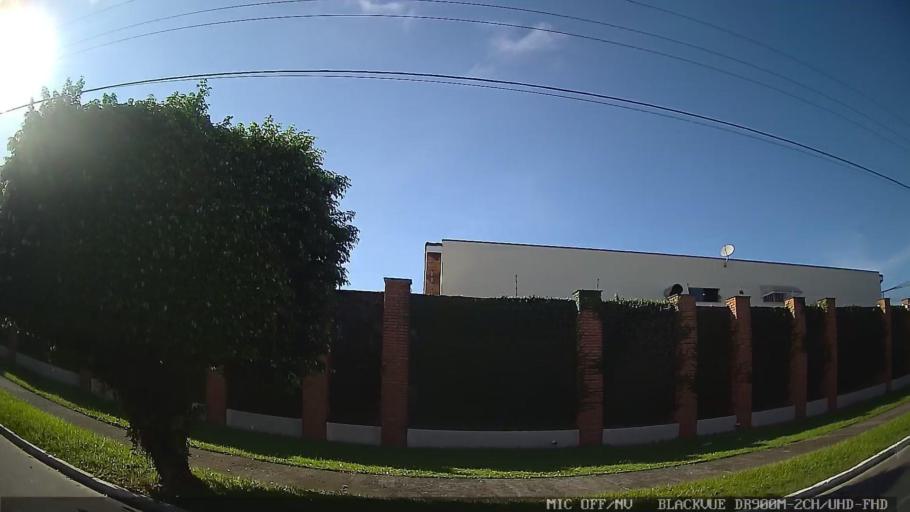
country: BR
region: Sao Paulo
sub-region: Peruibe
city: Peruibe
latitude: -24.2840
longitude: -46.9537
